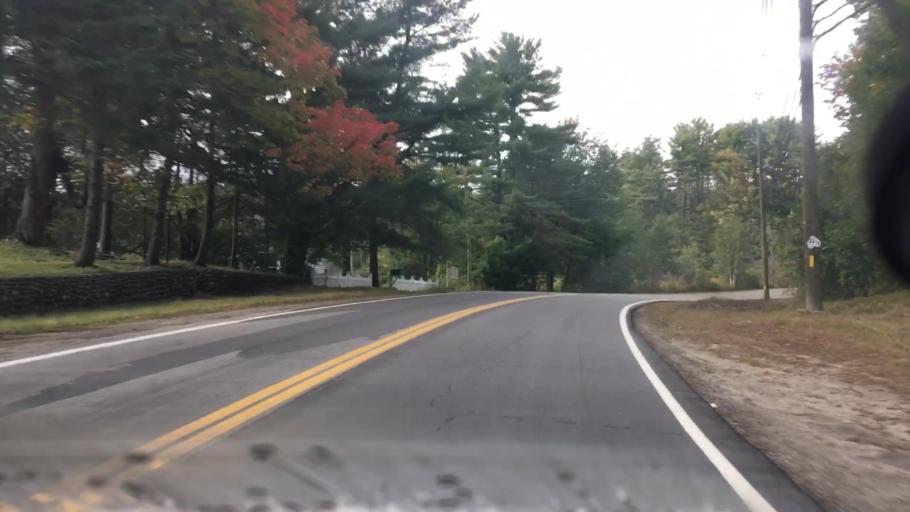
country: US
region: New Hampshire
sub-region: Carroll County
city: Wakefield
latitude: 43.5643
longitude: -71.0291
